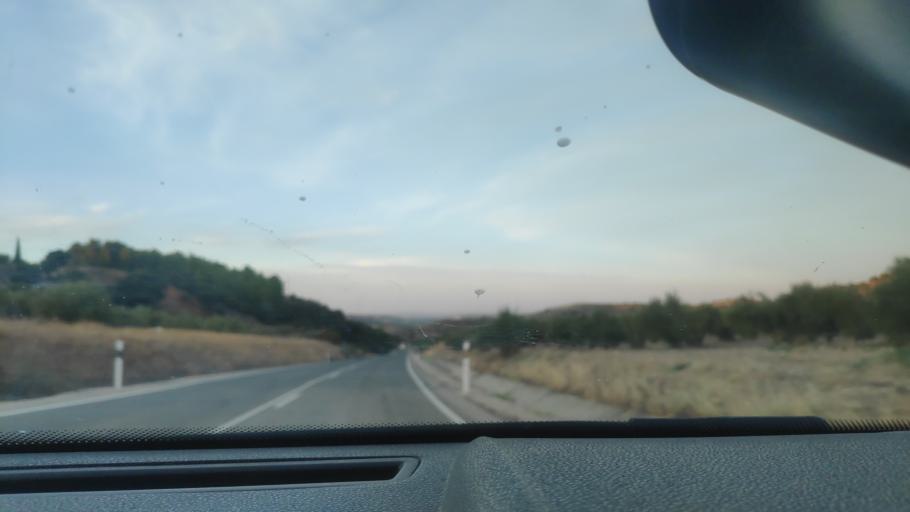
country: ES
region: Andalusia
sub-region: Provincia de Jaen
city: Villardompardo
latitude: 37.8313
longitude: -4.0488
